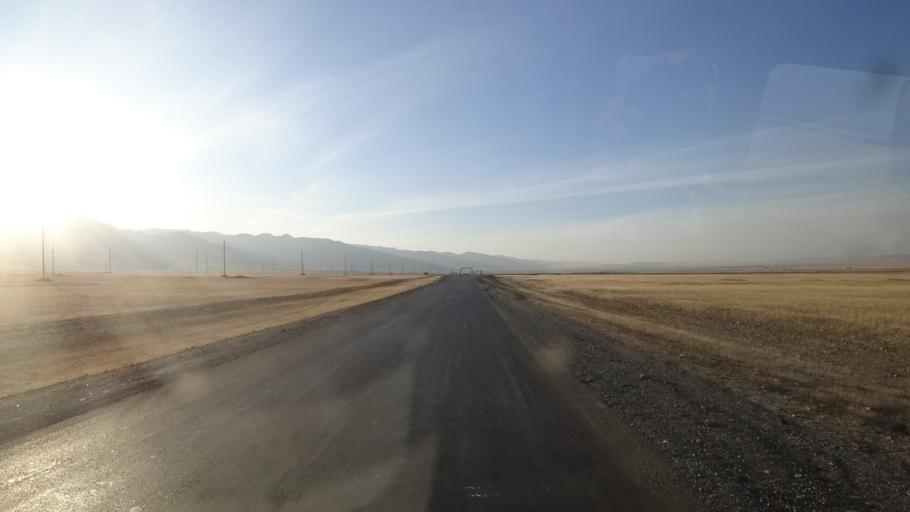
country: KZ
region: Zhambyl
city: Karatau
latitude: 42.9517
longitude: 70.6662
